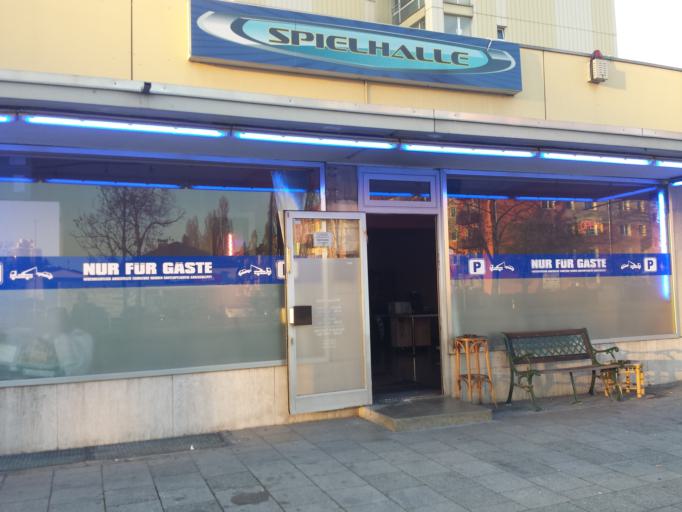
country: DE
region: Bavaria
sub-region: Upper Bavaria
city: Munich
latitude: 48.1868
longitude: 11.5595
